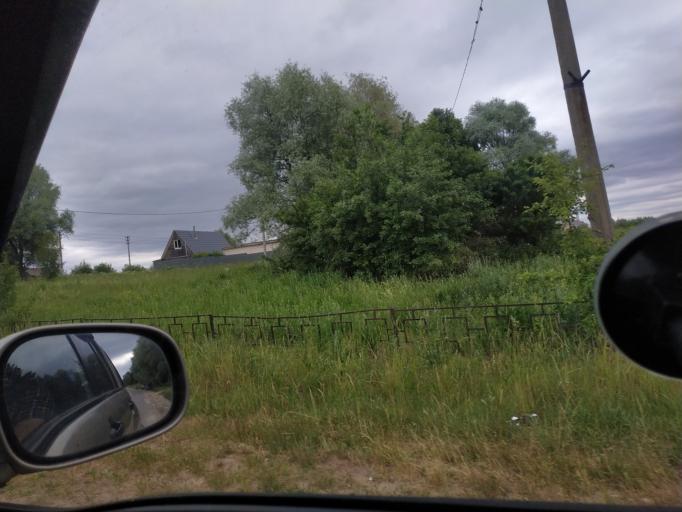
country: RU
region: Moskovskaya
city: Krasnoarmeysk
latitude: 56.0889
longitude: 38.2258
